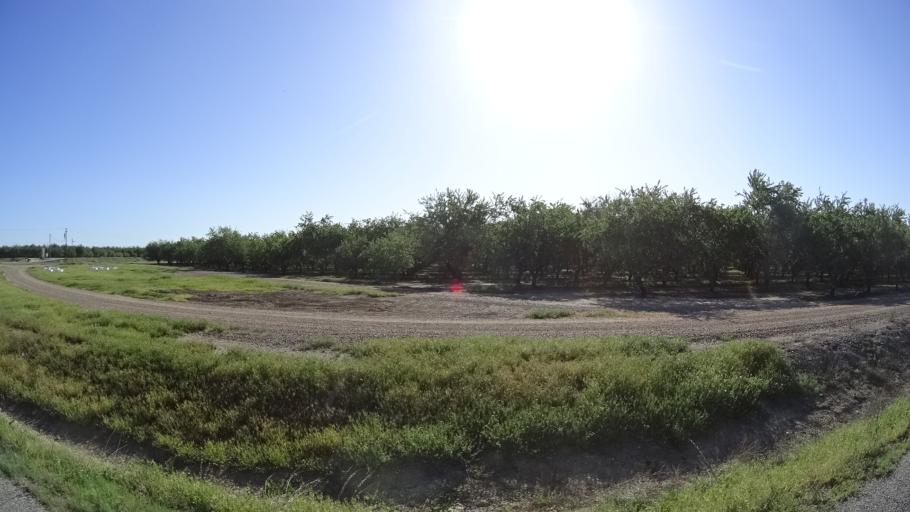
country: US
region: California
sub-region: Glenn County
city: Hamilton City
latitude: 39.7080
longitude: -122.0548
